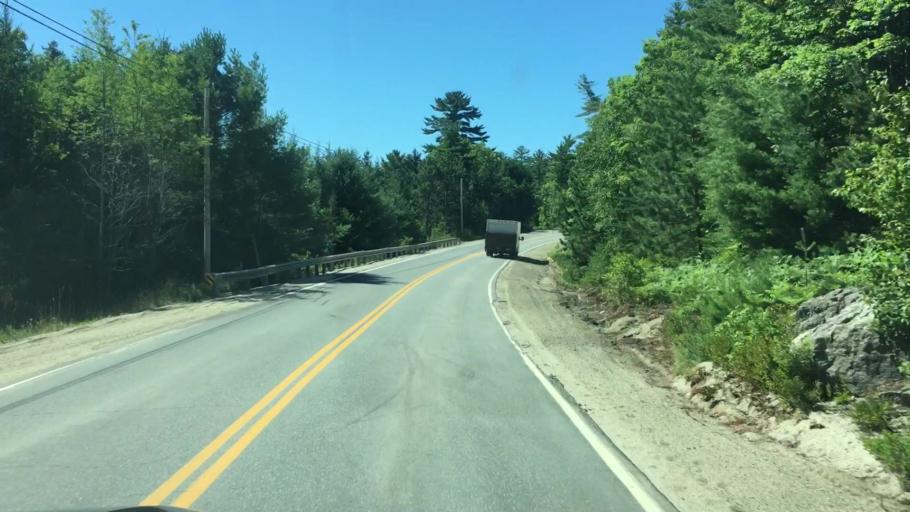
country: US
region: Maine
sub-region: Hancock County
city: Sedgwick
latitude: 44.3691
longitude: -68.5672
